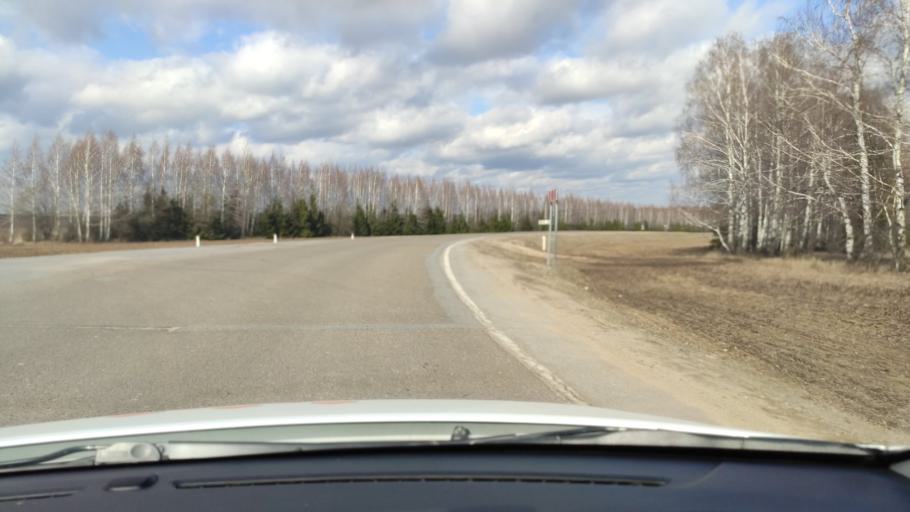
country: RU
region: Tatarstan
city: Vysokaya Gora
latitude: 56.1115
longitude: 49.1841
